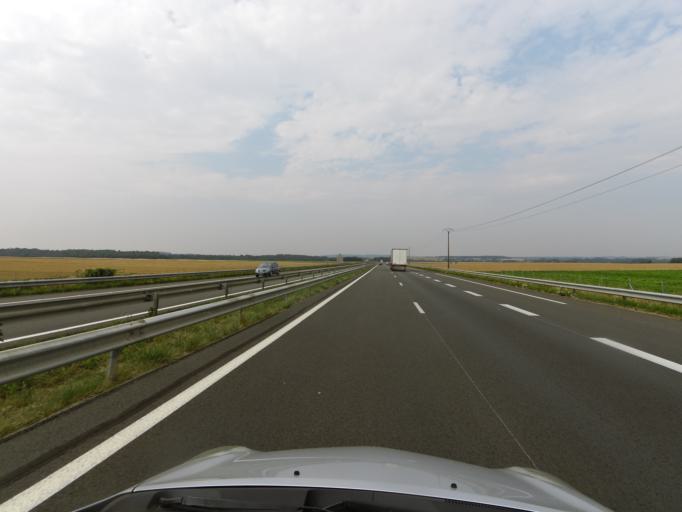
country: FR
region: Nord-Pas-de-Calais
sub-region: Departement du Nord
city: Marcoing
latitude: 50.0963
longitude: 3.1689
